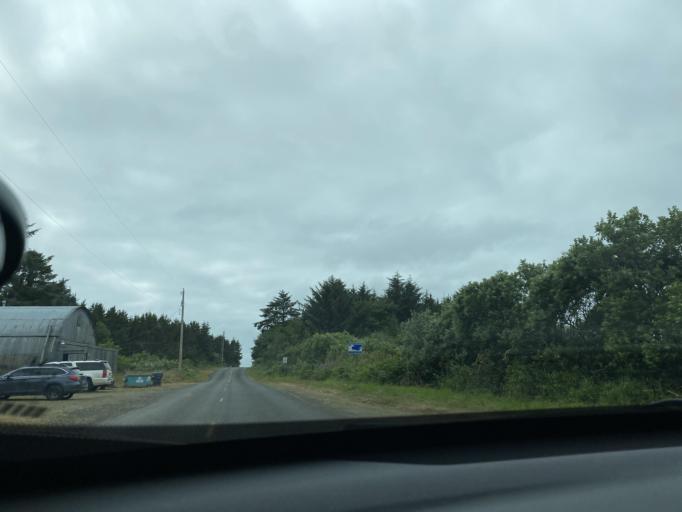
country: US
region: Washington
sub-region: Grays Harbor County
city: Ocean Shores
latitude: 47.1142
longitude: -124.1744
